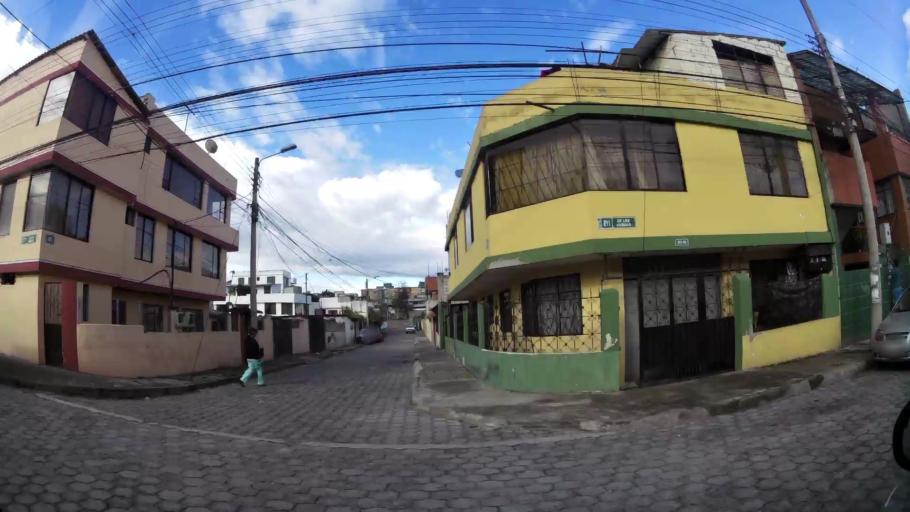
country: EC
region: Pichincha
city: Quito
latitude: -0.1312
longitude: -78.4703
